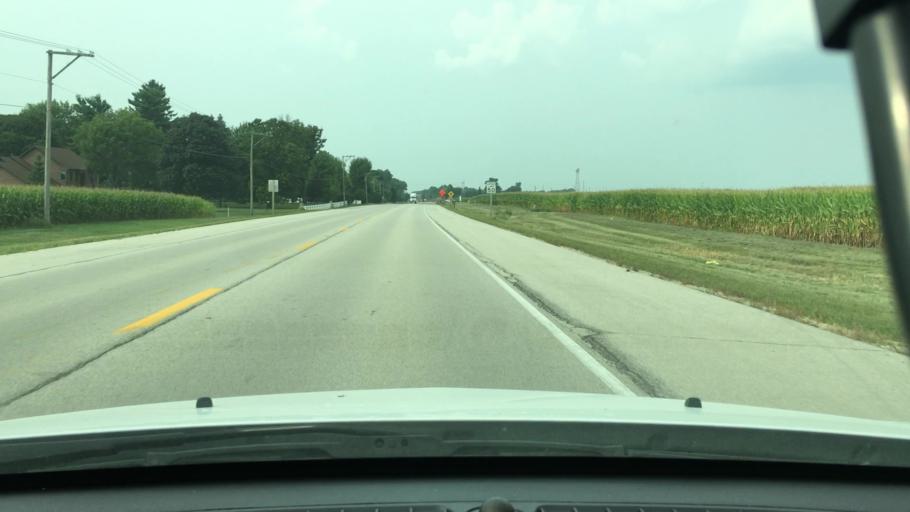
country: US
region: Illinois
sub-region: DeKalb County
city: DeKalb
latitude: 41.8890
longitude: -88.7537
